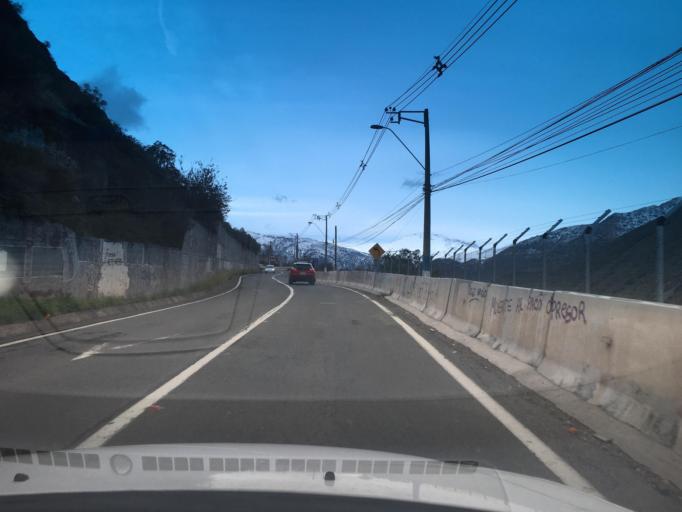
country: CL
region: Santiago Metropolitan
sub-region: Provincia de Cordillera
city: Puente Alto
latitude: -33.5783
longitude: -70.4201
